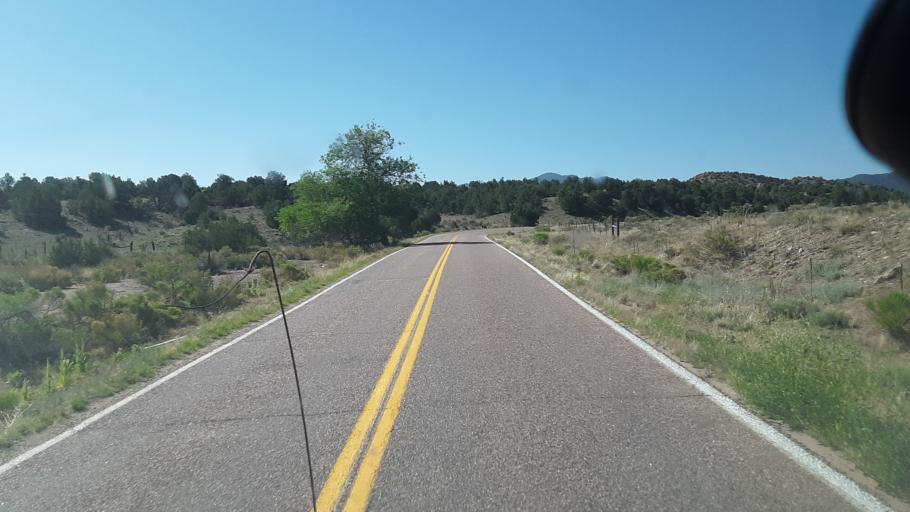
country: US
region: Colorado
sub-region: Fremont County
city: Canon City
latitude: 38.4560
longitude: -105.3739
